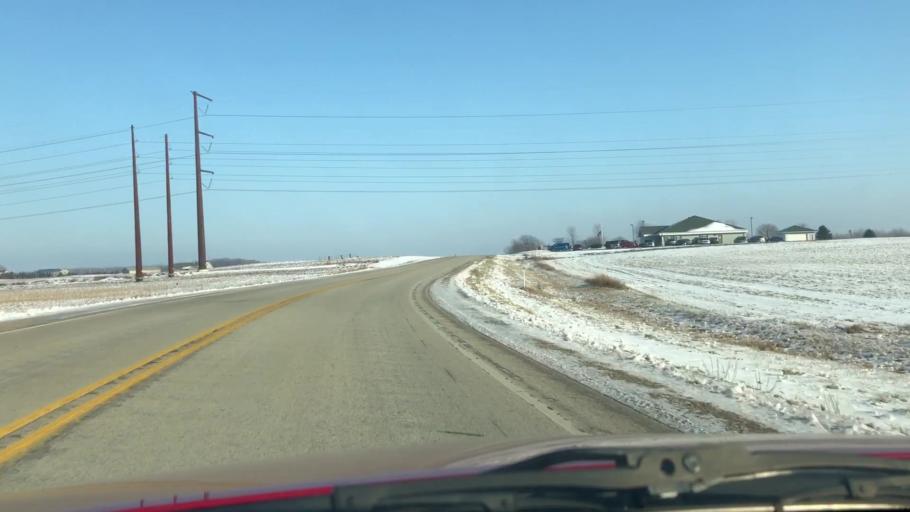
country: US
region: Wisconsin
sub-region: Outagamie County
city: Seymour
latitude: 44.4436
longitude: -88.3579
